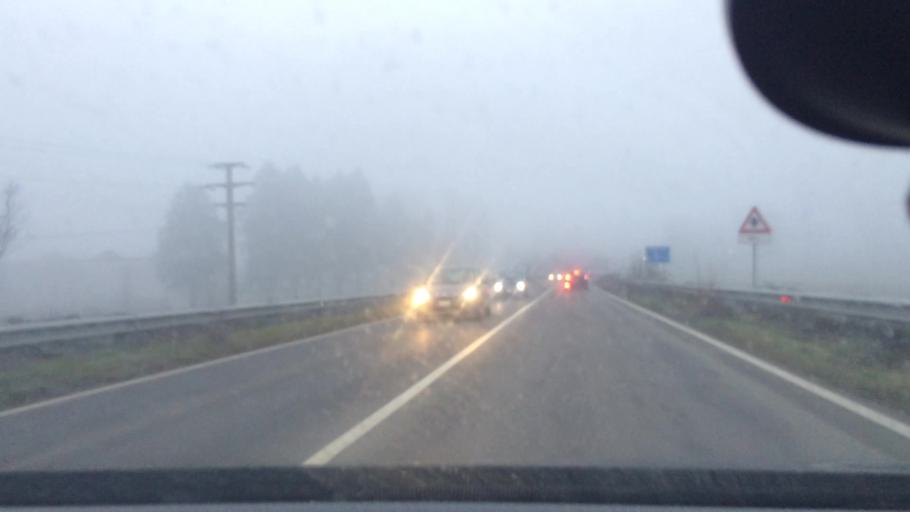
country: IT
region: Lombardy
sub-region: Citta metropolitana di Milano
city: Nerviano
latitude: 45.5596
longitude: 8.9917
